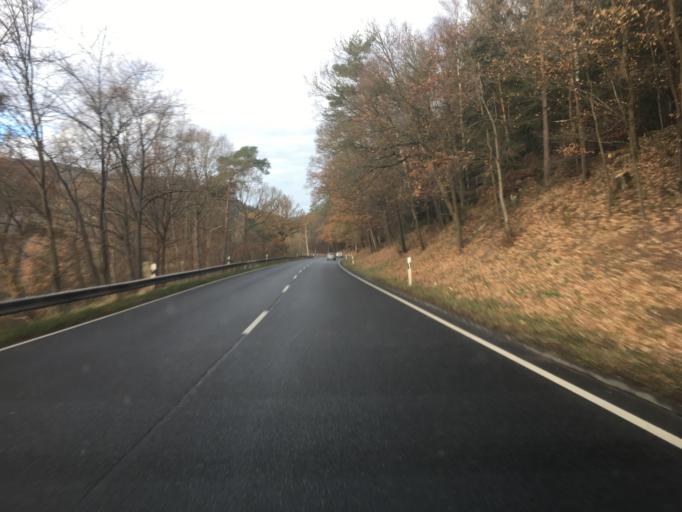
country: DE
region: North Rhine-Westphalia
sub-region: Regierungsbezirk Koln
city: Kall
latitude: 50.5597
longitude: 6.5392
